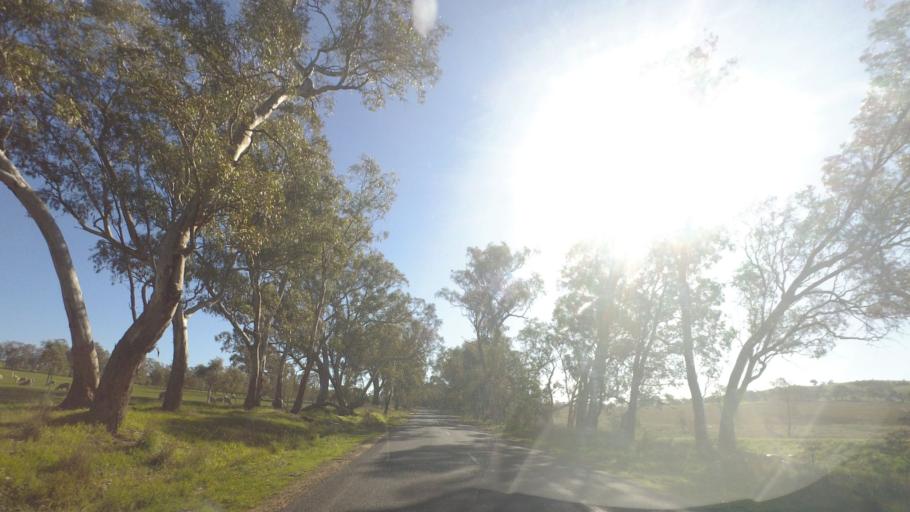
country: AU
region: Victoria
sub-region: Mount Alexander
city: Castlemaine
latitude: -36.9574
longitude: 144.3478
